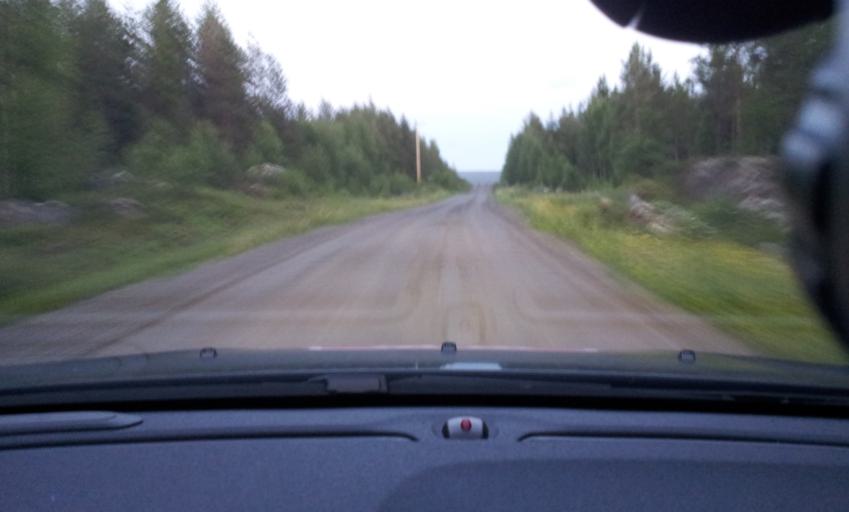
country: SE
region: Vaesternorrland
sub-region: Ange Kommun
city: Fransta
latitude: 62.8095
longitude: 16.0173
